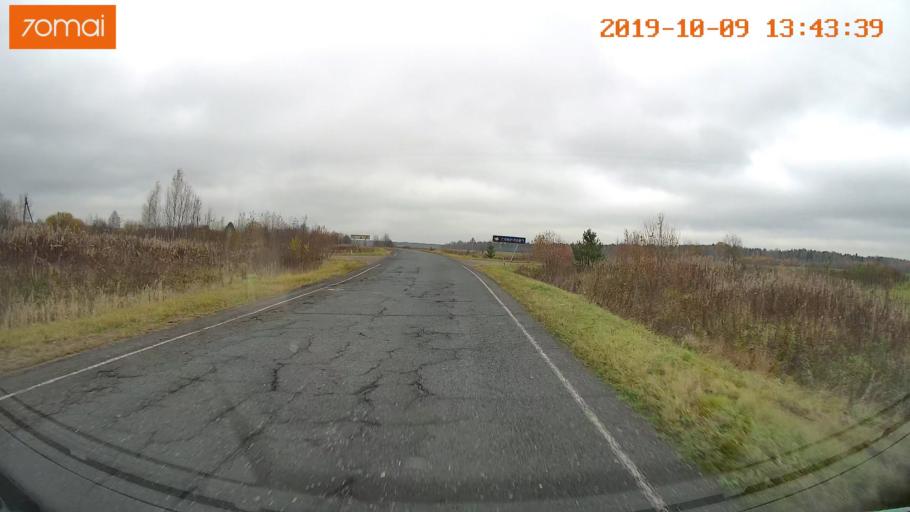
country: RU
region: Kostroma
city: Buy
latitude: 58.3586
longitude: 41.2026
